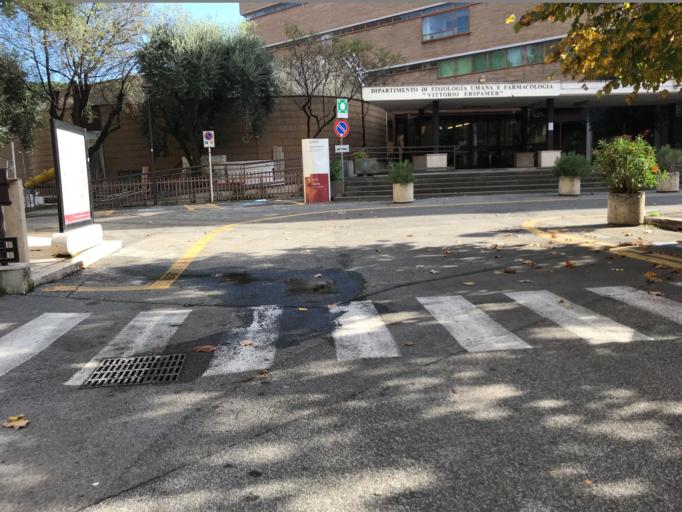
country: IT
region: Latium
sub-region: Citta metropolitana di Roma Capitale
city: Rome
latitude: 41.9032
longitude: 12.5173
